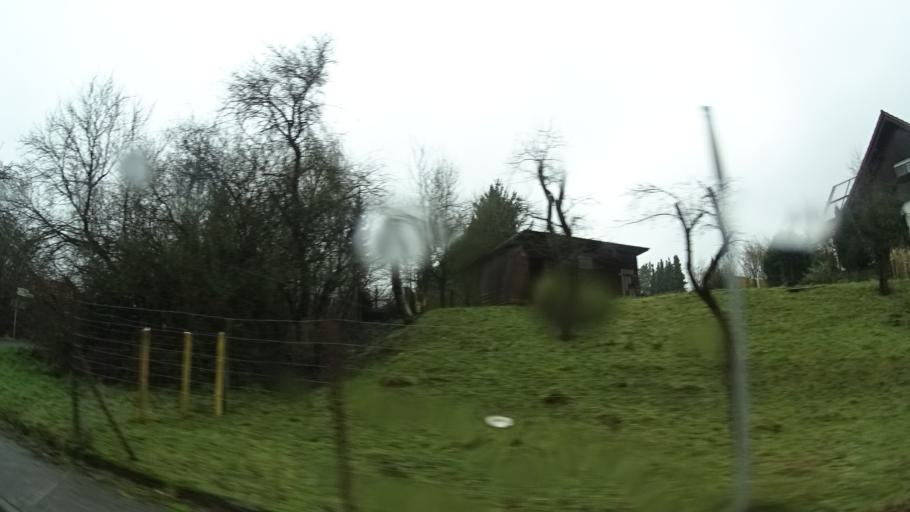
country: DE
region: Hesse
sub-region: Regierungsbezirk Kassel
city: Hofbieber
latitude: 50.5689
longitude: 9.8299
